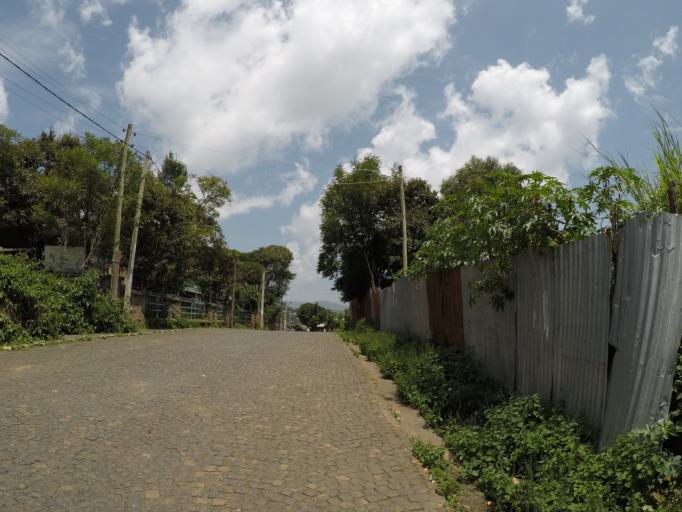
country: ET
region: Amhara
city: Gondar
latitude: 12.6121
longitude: 37.4714
